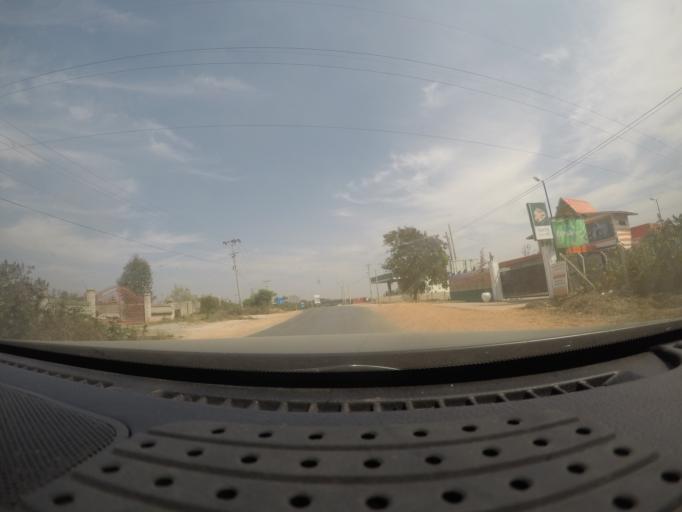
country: MM
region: Shan
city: Taunggyi
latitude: 20.6804
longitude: 96.6332
